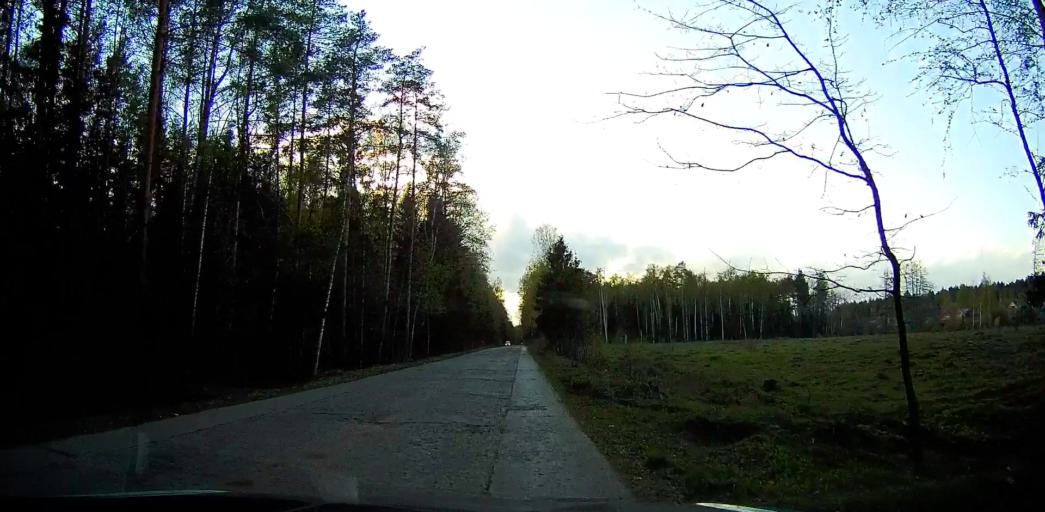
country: RU
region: Moskovskaya
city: Malyshevo
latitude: 55.5332
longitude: 38.3982
